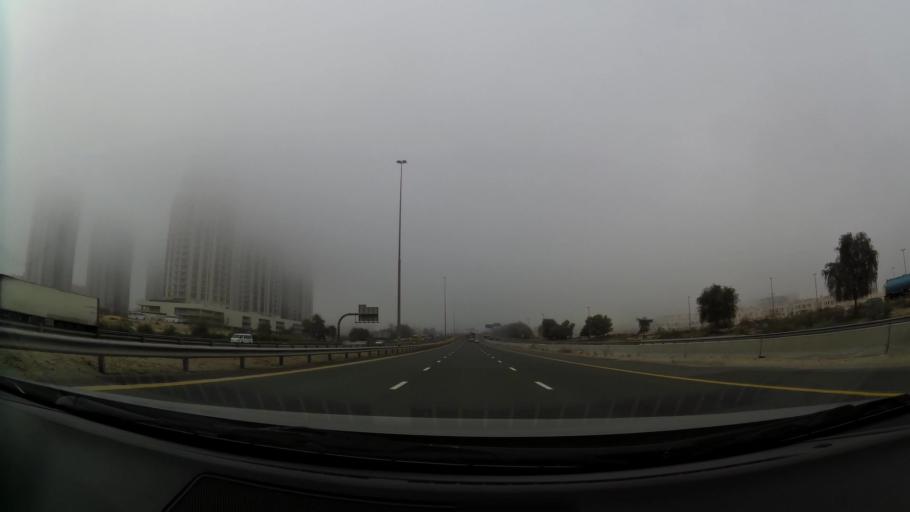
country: AE
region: Dubai
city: Dubai
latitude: 25.1147
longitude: 55.3692
